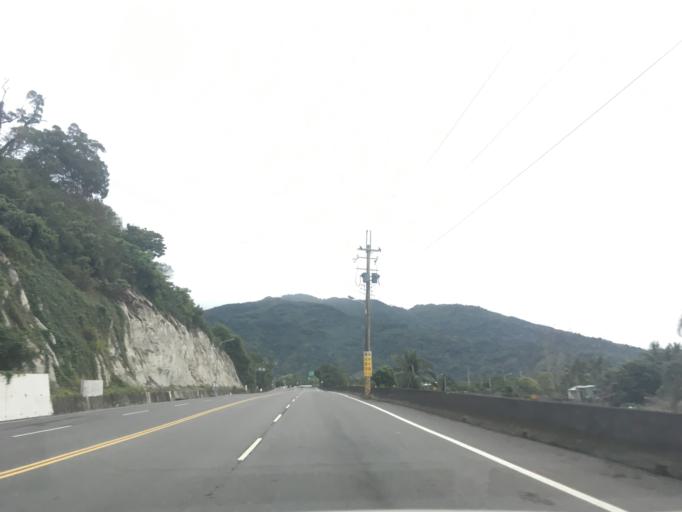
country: TW
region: Taiwan
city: Taitung City
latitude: 22.7533
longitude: 121.0537
